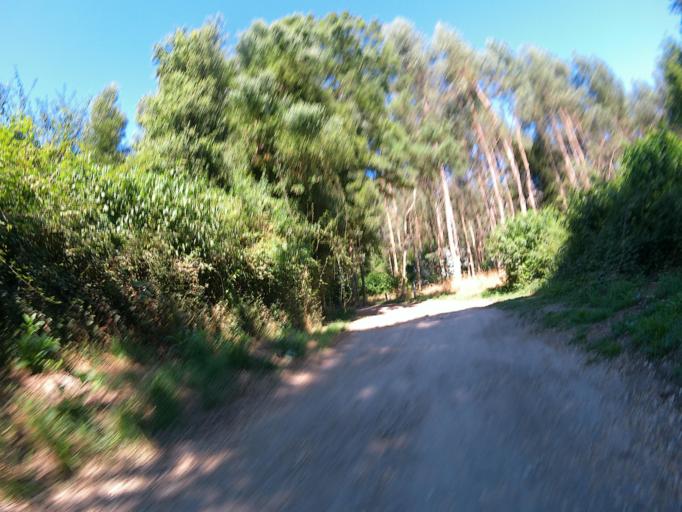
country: PT
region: Viana do Castelo
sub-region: Ponte de Lima
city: Ponte de Lima
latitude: 41.7590
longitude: -8.6188
